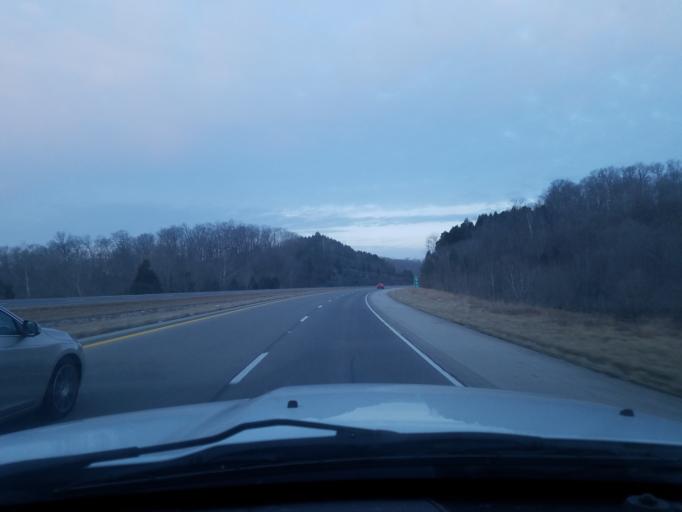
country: US
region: Indiana
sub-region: Harrison County
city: Corydon
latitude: 38.2347
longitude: -86.2355
